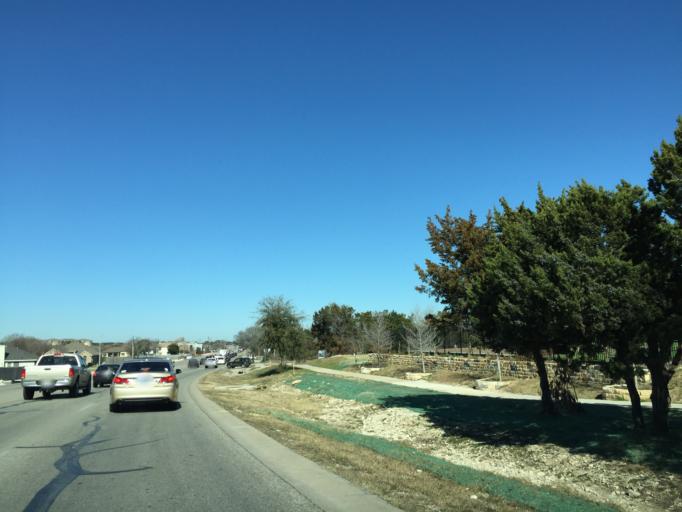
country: US
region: Texas
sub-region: Williamson County
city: Leander
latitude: 30.5530
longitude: -97.8570
